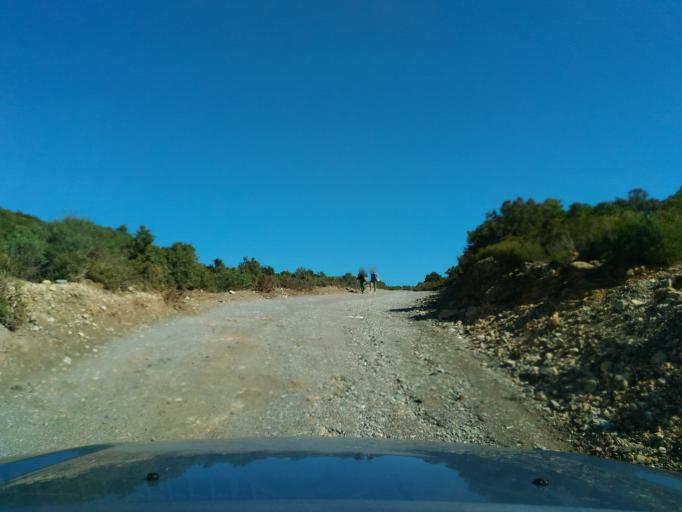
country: FR
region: Corsica
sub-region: Departement de la Haute-Corse
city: Brando
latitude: 42.9705
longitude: 9.4535
